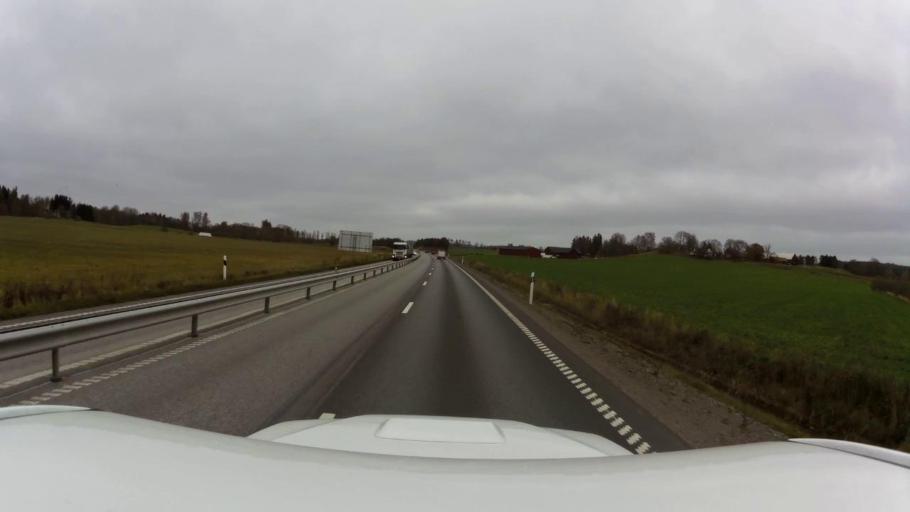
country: SE
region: OEstergoetland
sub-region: Kinda Kommun
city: Rimforsa
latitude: 58.1418
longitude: 15.6811
